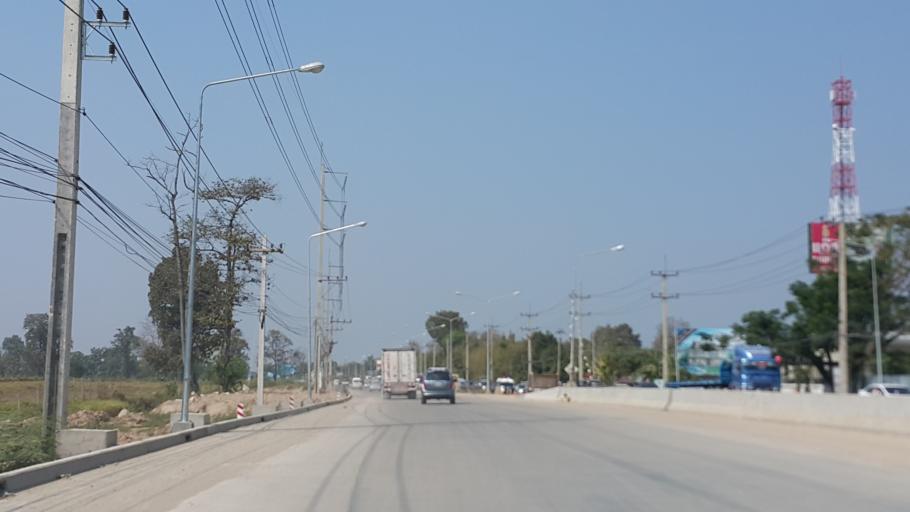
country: TH
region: Chiang Mai
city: Chiang Mai
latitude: 18.8709
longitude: 98.9632
